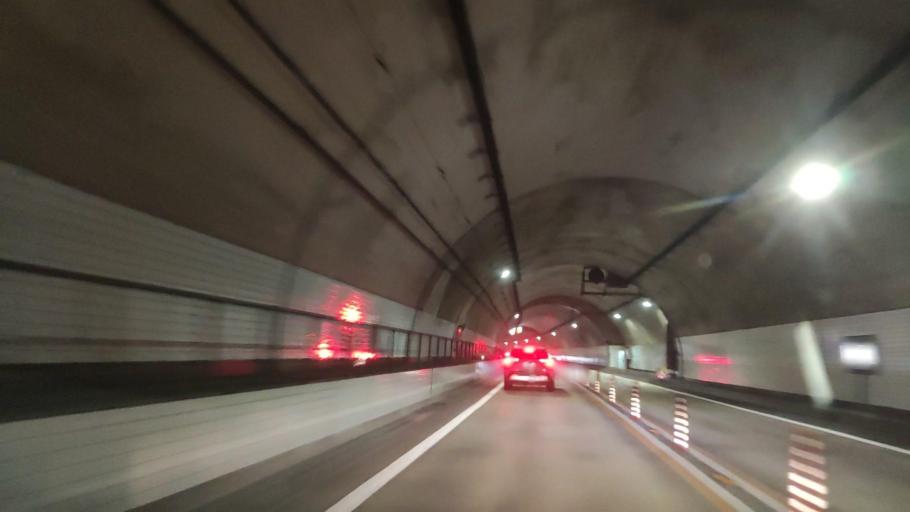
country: JP
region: Kyoto
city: Miyazu
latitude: 35.5565
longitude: 135.1262
